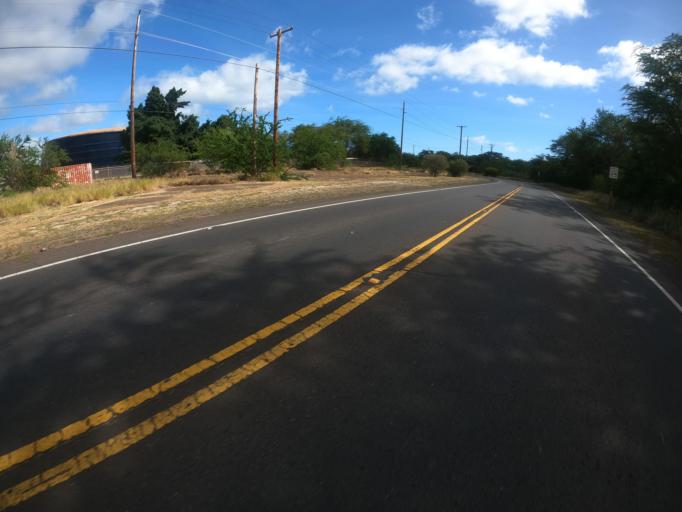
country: US
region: Hawaii
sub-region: Honolulu County
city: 'Ewa Villages
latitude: 21.3294
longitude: -158.0409
